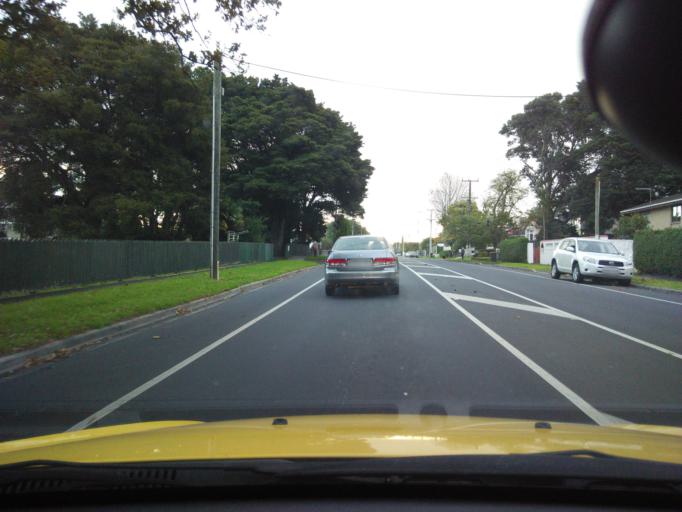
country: NZ
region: Auckland
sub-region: Auckland
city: Auckland
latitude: -36.9147
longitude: 174.7883
